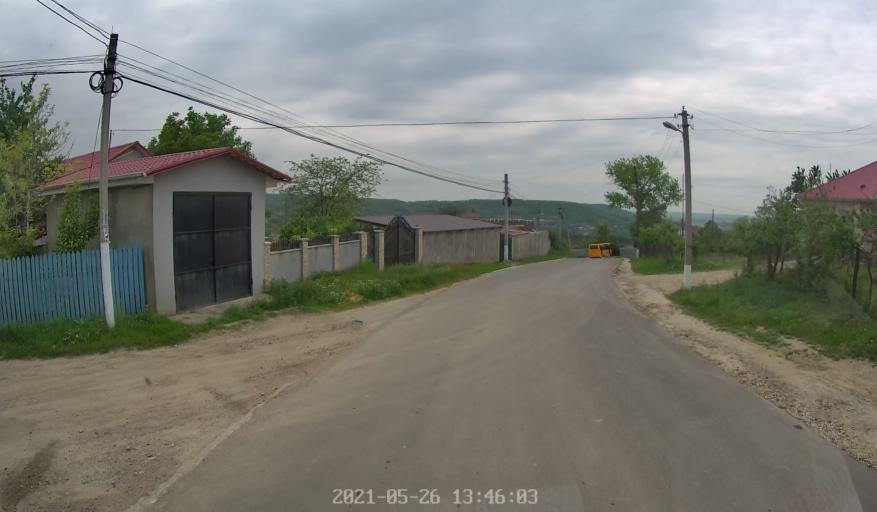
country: MD
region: Hincesti
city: Dancu
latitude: 46.7687
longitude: 28.3597
